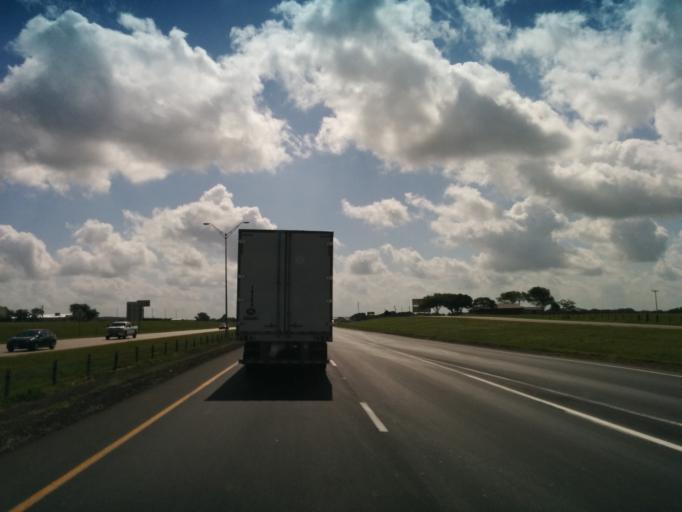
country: US
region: Texas
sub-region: Colorado County
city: Weimar
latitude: 29.6919
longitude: -96.7733
